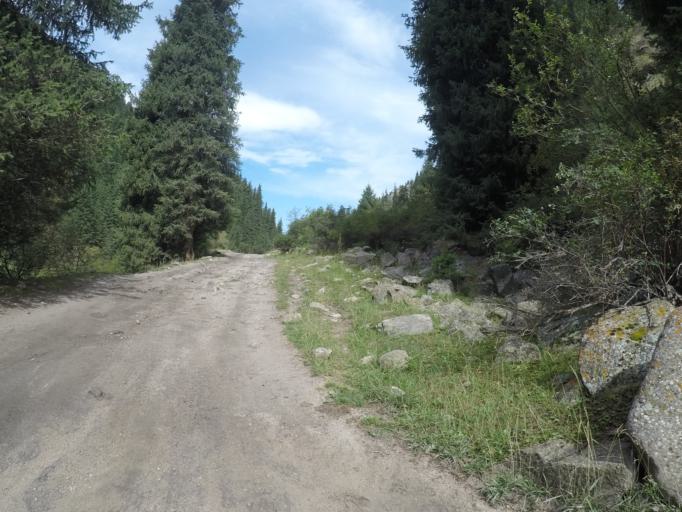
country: KG
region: Ysyk-Koel
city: Teploklyuchenka
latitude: 42.4367
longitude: 78.5613
